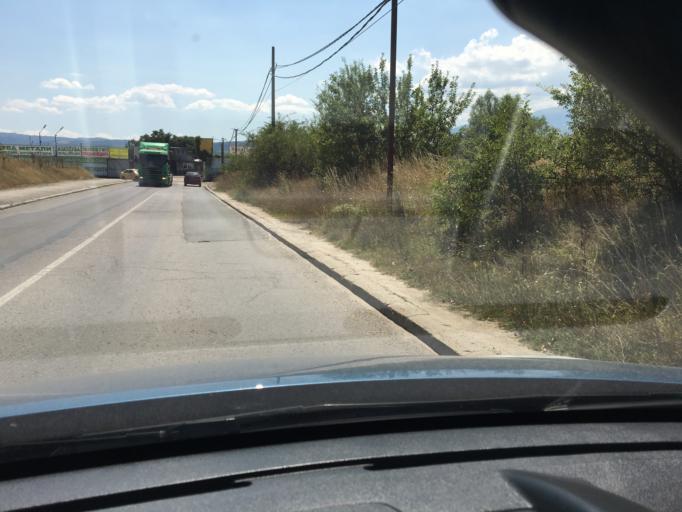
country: BG
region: Sofia-Capital
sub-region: Stolichna Obshtina
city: Sofia
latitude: 42.6377
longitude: 23.3977
